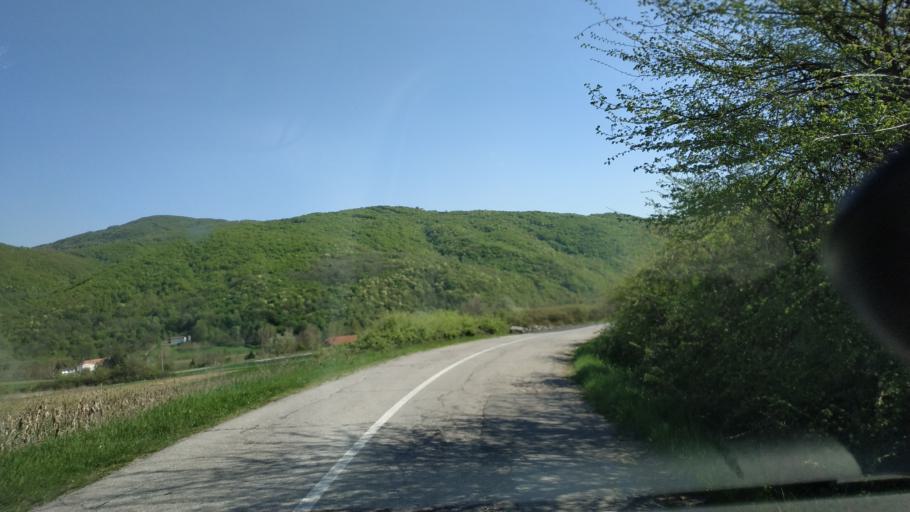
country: RS
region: Central Serbia
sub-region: Nisavski Okrug
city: Nis
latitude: 43.4308
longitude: 21.8487
